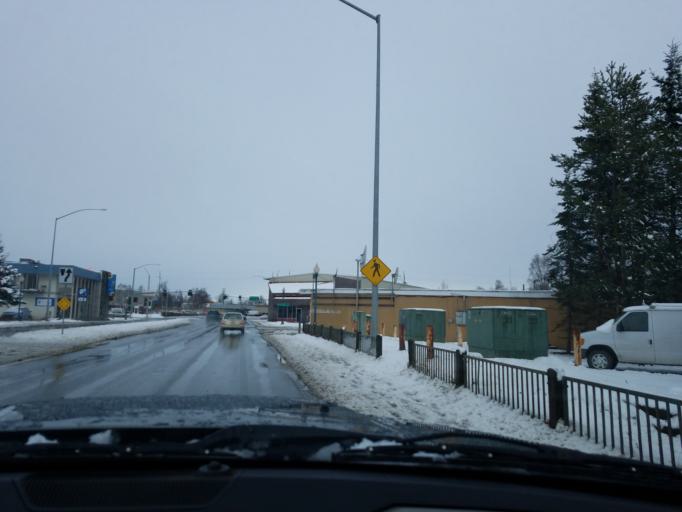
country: US
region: Alaska
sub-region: Anchorage Municipality
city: Anchorage
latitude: 61.1844
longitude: -149.9253
